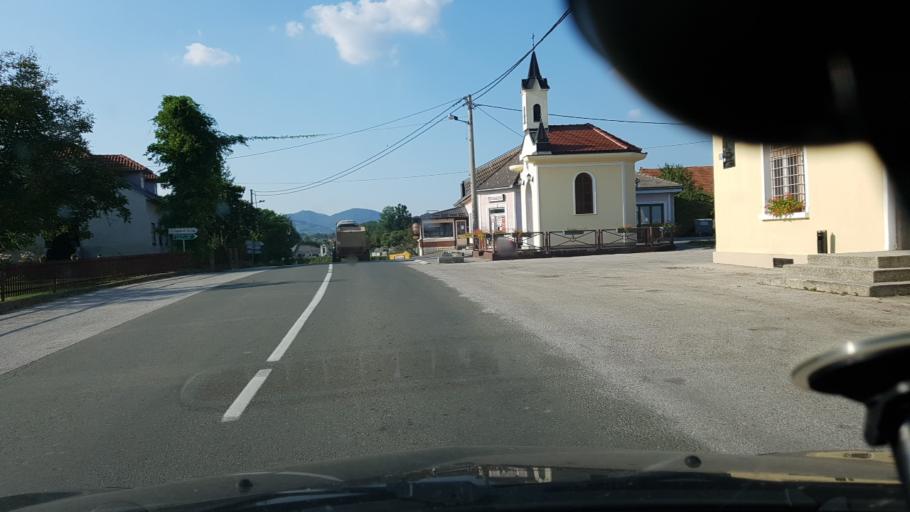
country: SI
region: Bistrica ob Sotli
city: Bistrica ob Sotli
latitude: 45.9850
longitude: 15.7276
